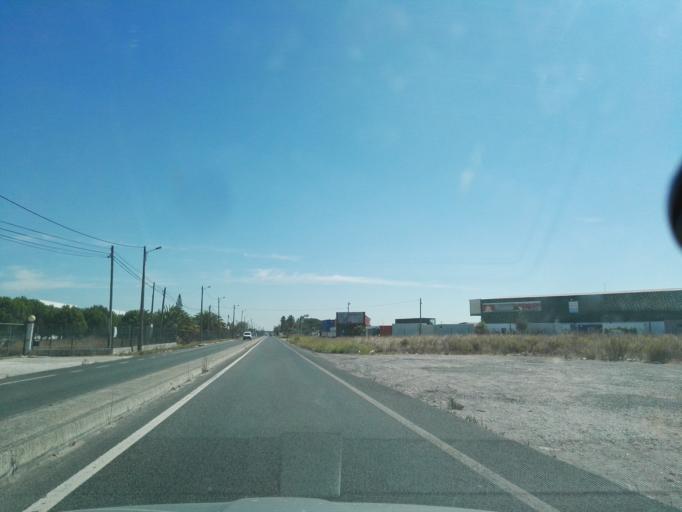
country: PT
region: Santarem
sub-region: Benavente
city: Samora Correia
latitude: 38.9175
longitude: -8.8689
